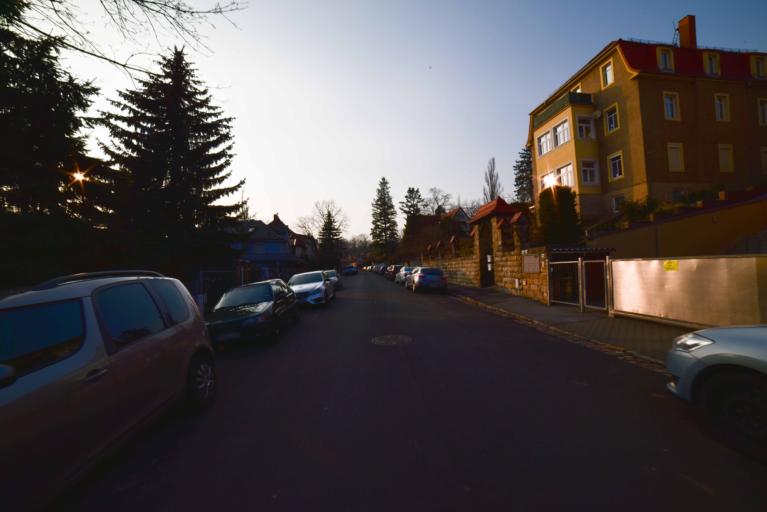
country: DE
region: Saxony
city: Albertstadt
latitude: 51.0966
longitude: 13.7266
